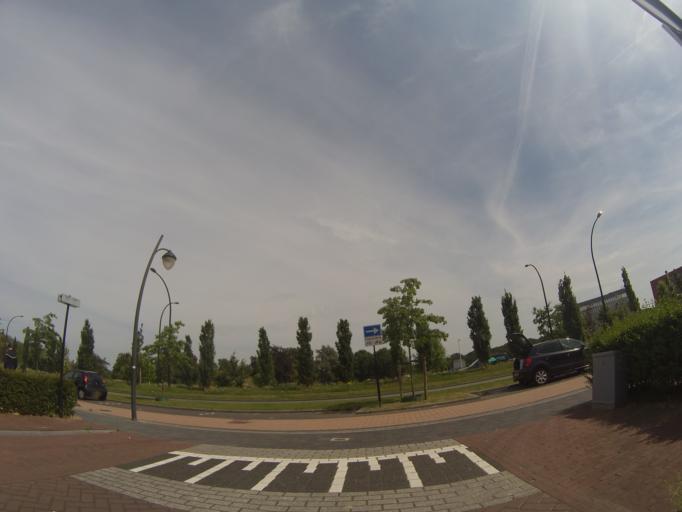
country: NL
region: Utrecht
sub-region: Gemeente Amersfoort
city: Randenbroek
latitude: 52.1910
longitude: 5.4345
